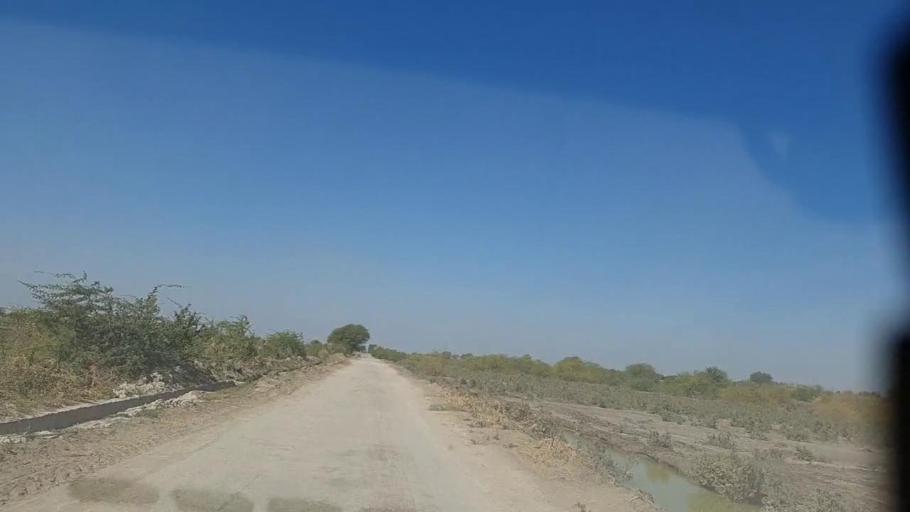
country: PK
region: Sindh
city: Digri
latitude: 25.1707
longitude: 69.0628
